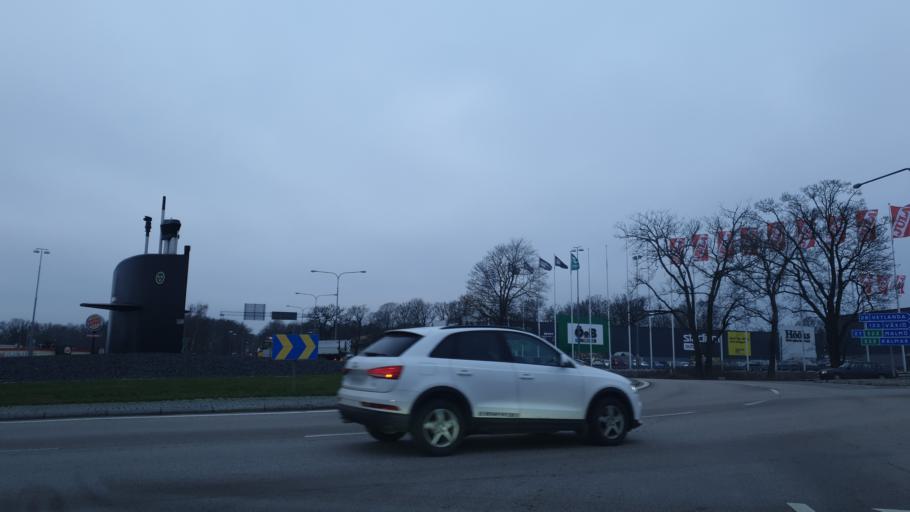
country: SE
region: Blekinge
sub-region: Karlskrona Kommun
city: Rodeby
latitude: 56.2034
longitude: 15.6402
